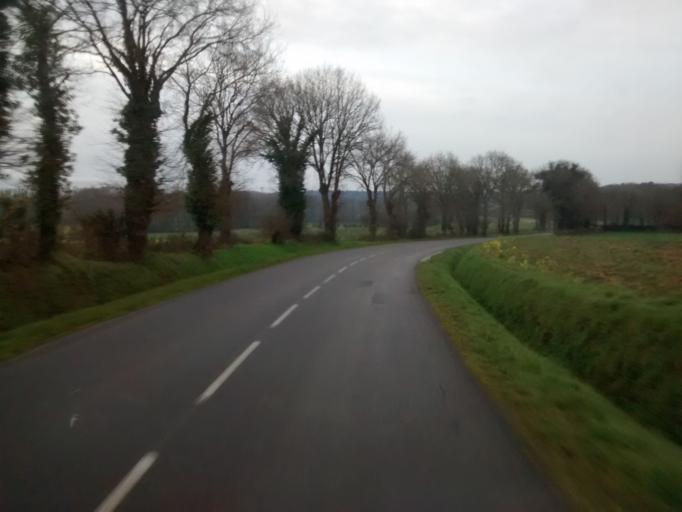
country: FR
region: Brittany
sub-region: Departement du Morbihan
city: Malestroit
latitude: 47.8202
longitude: -2.4002
